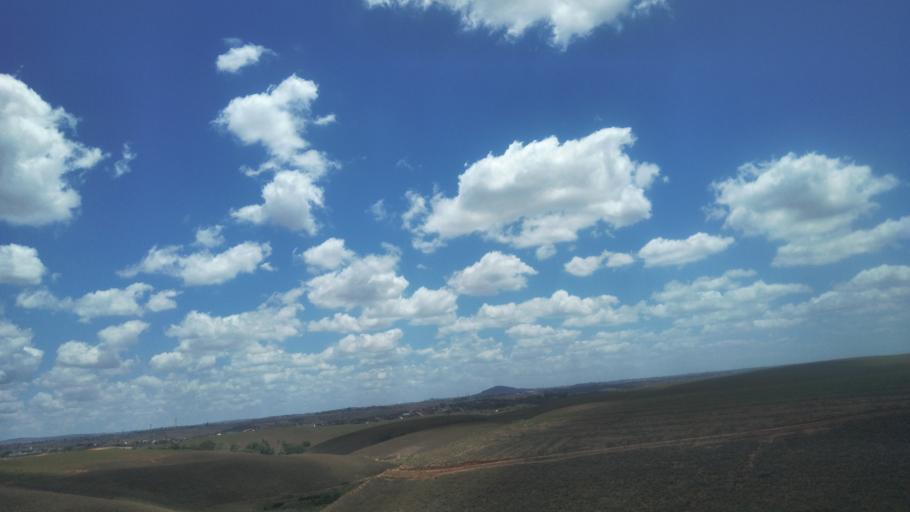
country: BR
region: Pernambuco
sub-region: Nazare Da Mata
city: Nazare da Mata
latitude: -7.7274
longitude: -35.2431
